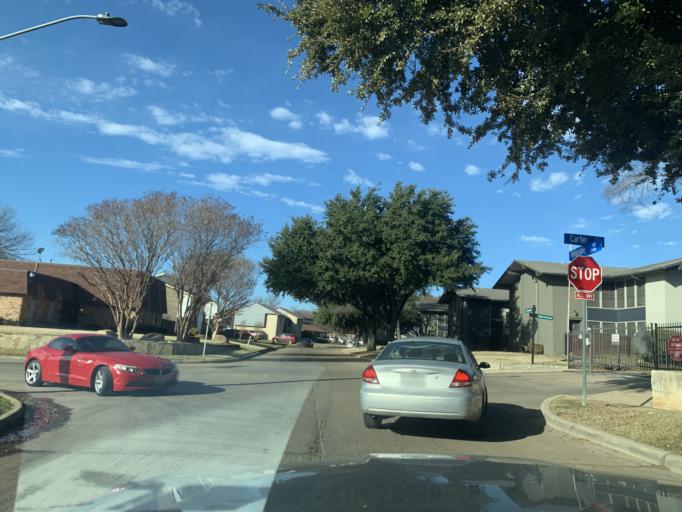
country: US
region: Texas
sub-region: Tarrant County
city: Arlington
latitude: 32.7325
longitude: -97.0660
